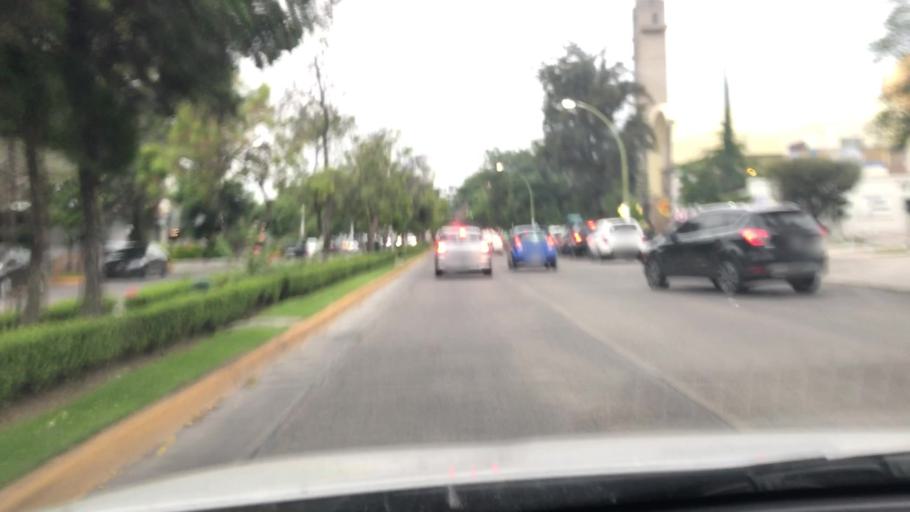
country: MX
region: Jalisco
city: Guadalajara
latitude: 20.6658
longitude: -103.4054
